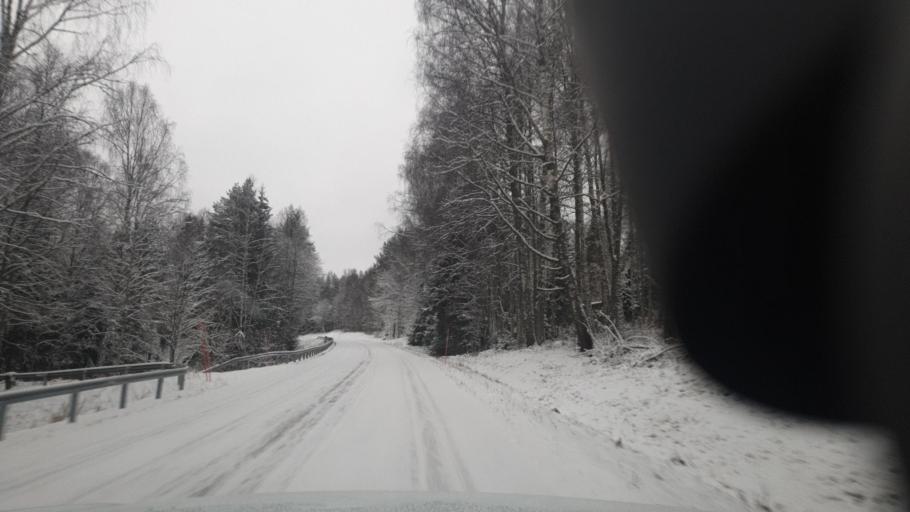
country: NO
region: Hedmark
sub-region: Eidskog
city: Skotterud
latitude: 59.7655
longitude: 12.0484
